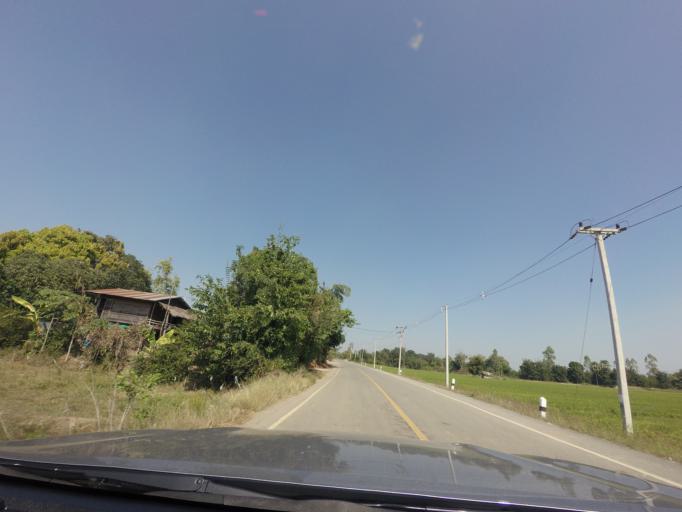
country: TH
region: Sukhothai
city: Si Samrong
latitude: 17.1526
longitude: 99.7701
